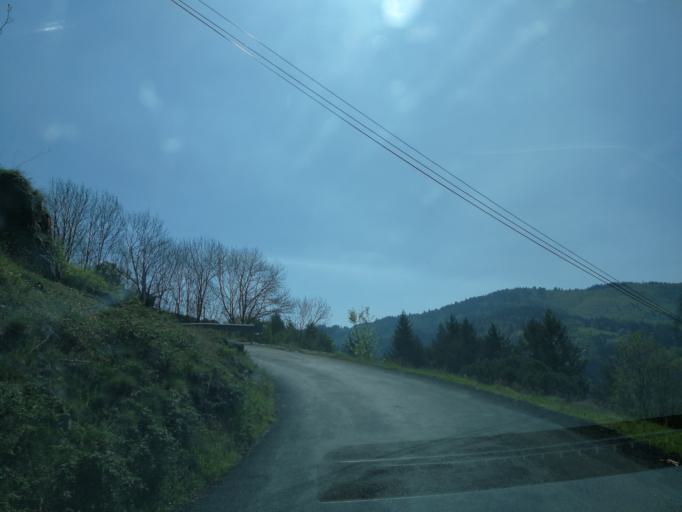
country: FR
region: Rhone-Alpes
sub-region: Departement de l'Ardeche
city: Le Cheylard
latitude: 44.9161
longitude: 4.4246
